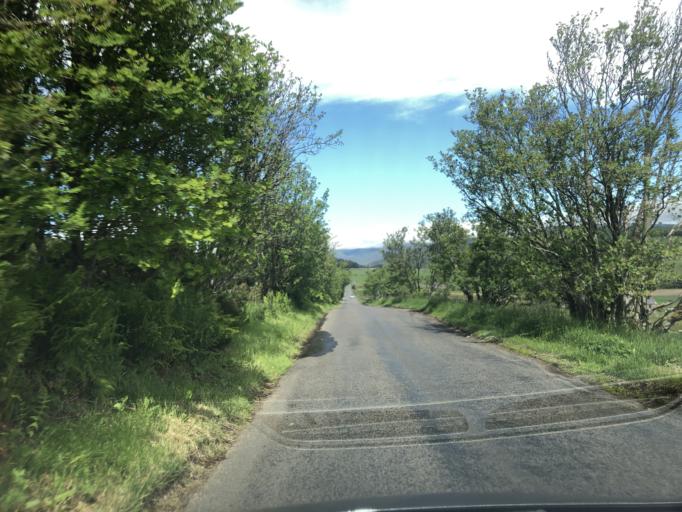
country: GB
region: Scotland
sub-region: Angus
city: Kirriemuir
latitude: 56.7470
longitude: -3.0133
